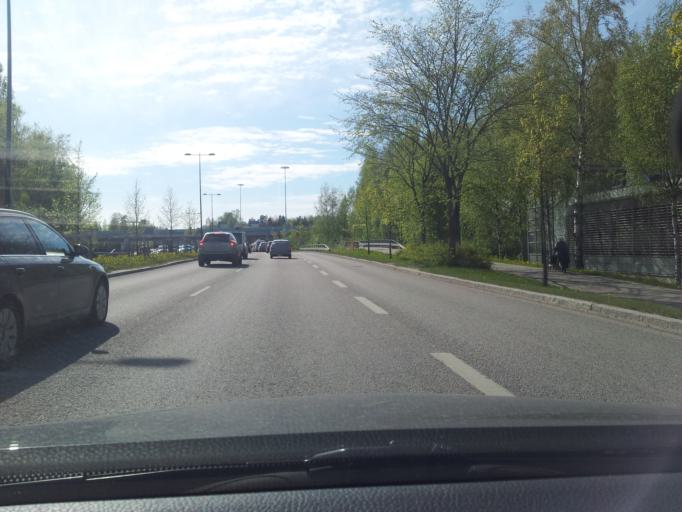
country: FI
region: Uusimaa
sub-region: Helsinki
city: Koukkuniemi
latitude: 60.1708
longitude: 24.7575
